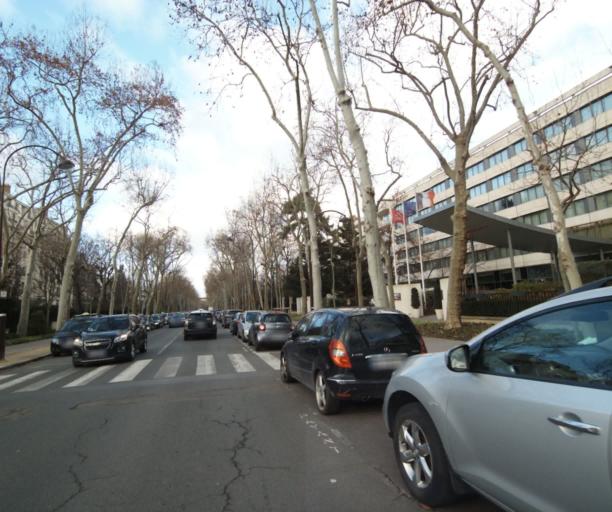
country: FR
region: Ile-de-France
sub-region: Departement des Hauts-de-Seine
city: Neuilly-sur-Seine
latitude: 48.8898
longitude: 2.2765
